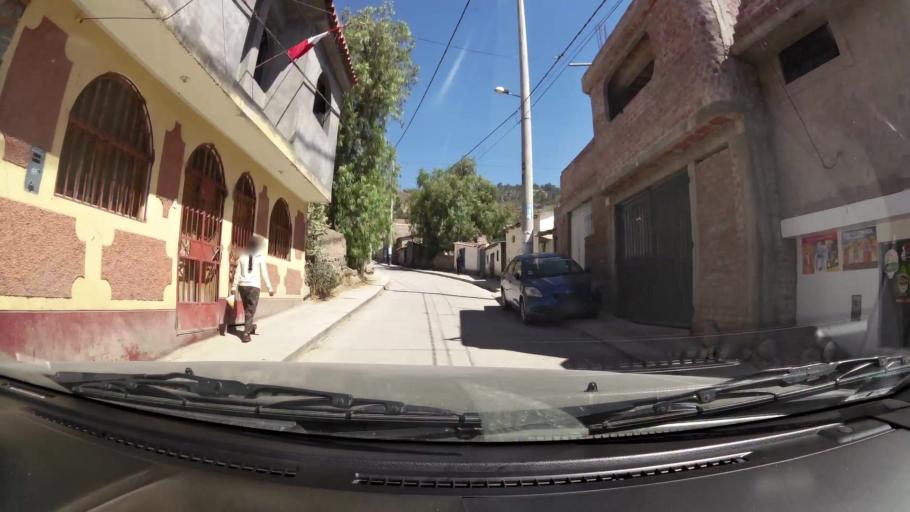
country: PE
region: Ayacucho
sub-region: Provincia de Huamanga
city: Ayacucho
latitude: -13.1687
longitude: -74.2347
